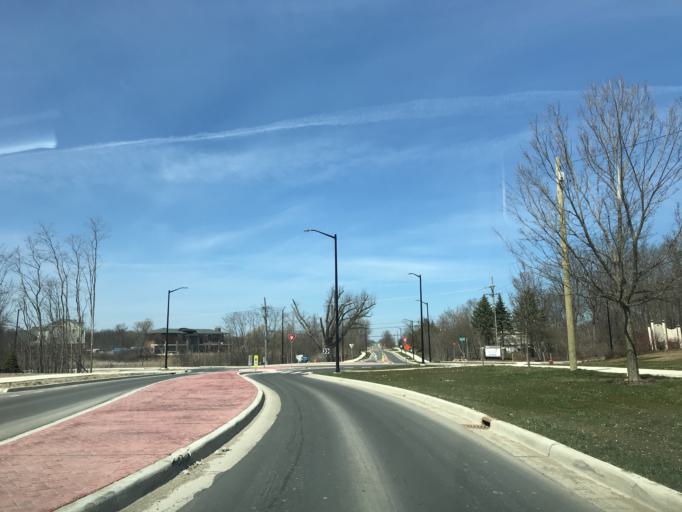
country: US
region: Michigan
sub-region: Washtenaw County
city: Ann Arbor
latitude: 42.3163
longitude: -83.7076
